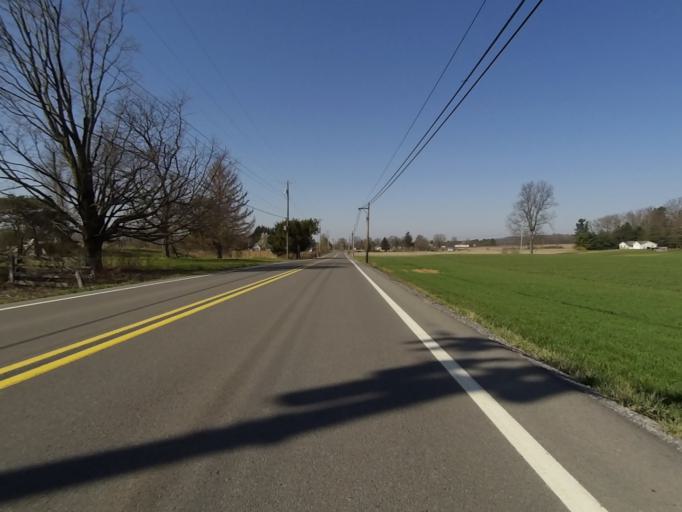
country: US
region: Pennsylvania
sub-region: Centre County
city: Park Forest Village
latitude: 40.7763
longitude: -77.9007
